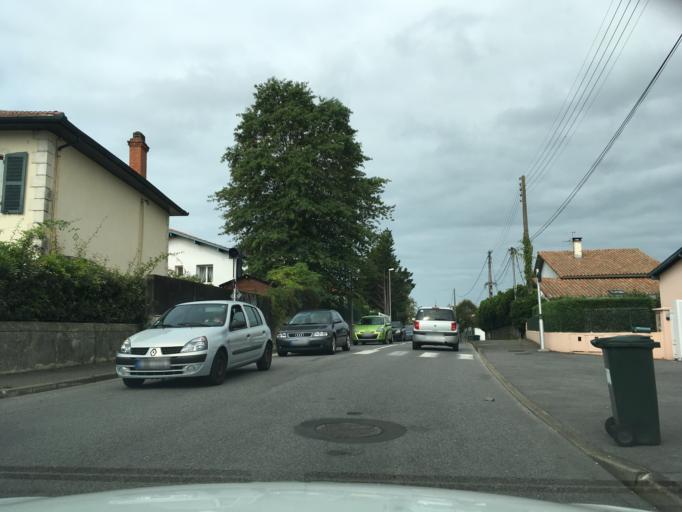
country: FR
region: Aquitaine
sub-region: Departement des Pyrenees-Atlantiques
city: Anglet
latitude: 43.4927
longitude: -1.5061
